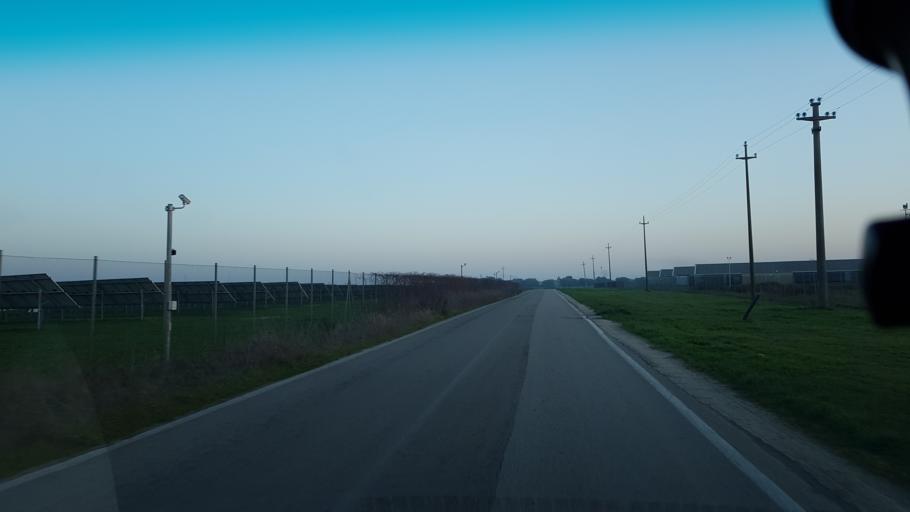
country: IT
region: Apulia
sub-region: Provincia di Brindisi
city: Mesagne
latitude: 40.6008
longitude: 17.7932
